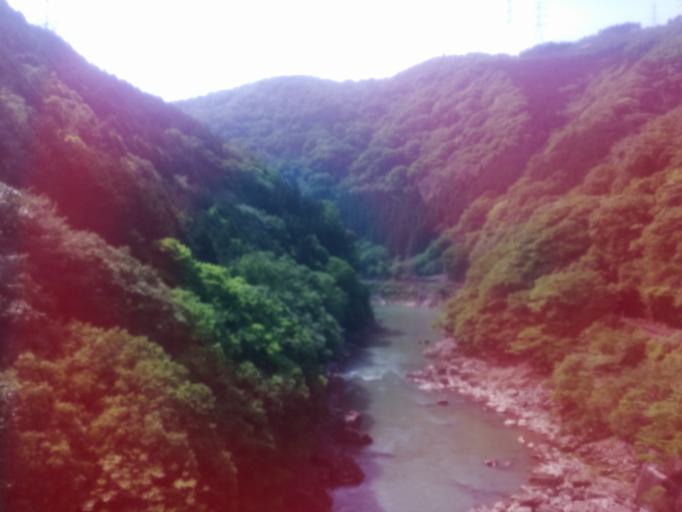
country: JP
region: Kyoto
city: Kameoka
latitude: 35.0223
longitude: 135.6254
